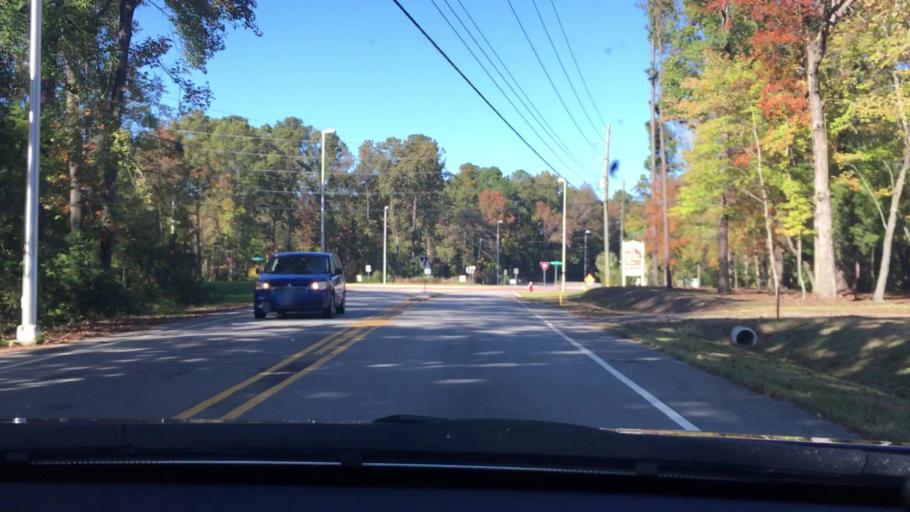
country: US
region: South Carolina
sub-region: Lexington County
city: Irmo
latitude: 34.1292
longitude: -81.1776
